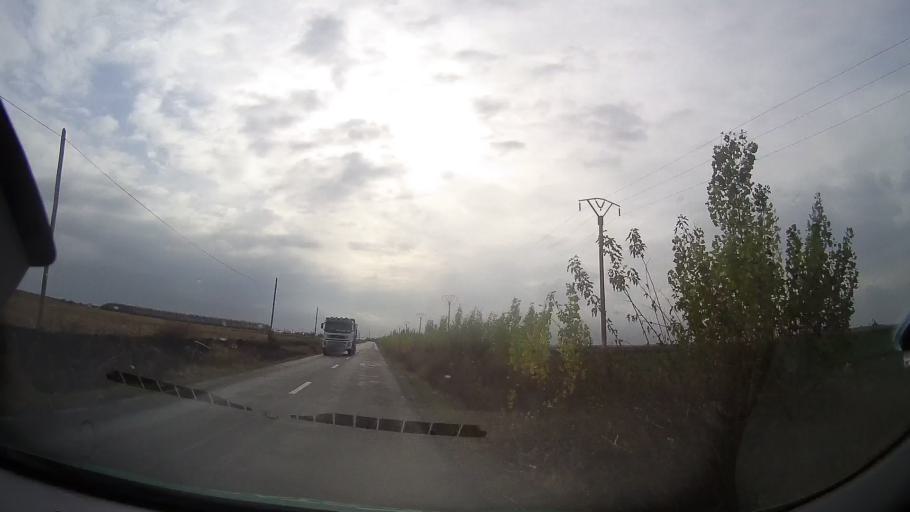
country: RO
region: Ialomita
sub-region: Comuna Maia
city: Maia
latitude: 44.7215
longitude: 26.3909
